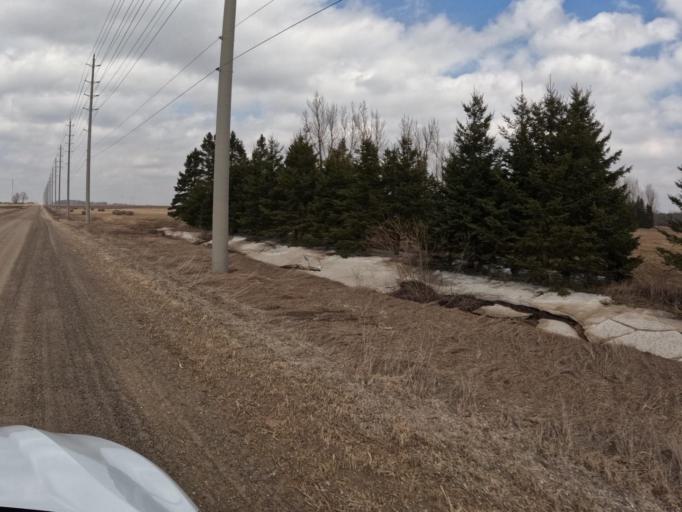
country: CA
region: Ontario
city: Shelburne
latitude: 44.0367
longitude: -80.3166
